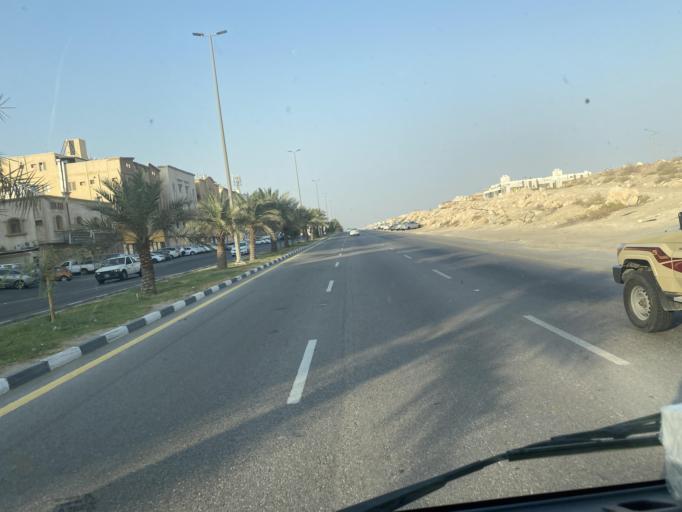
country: SA
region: Eastern Province
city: Dammam
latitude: 26.3586
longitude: 50.0642
